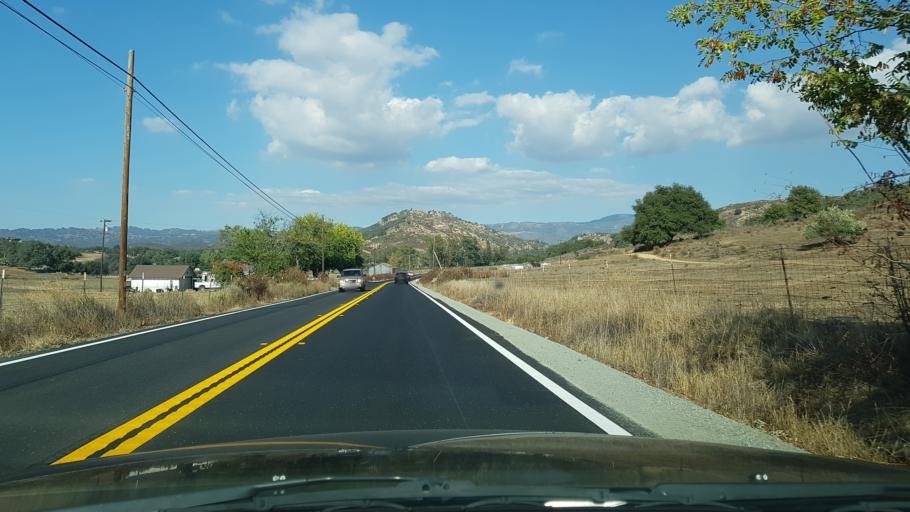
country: US
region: California
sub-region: San Diego County
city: San Diego Country Estates
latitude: 33.0765
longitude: -116.7180
